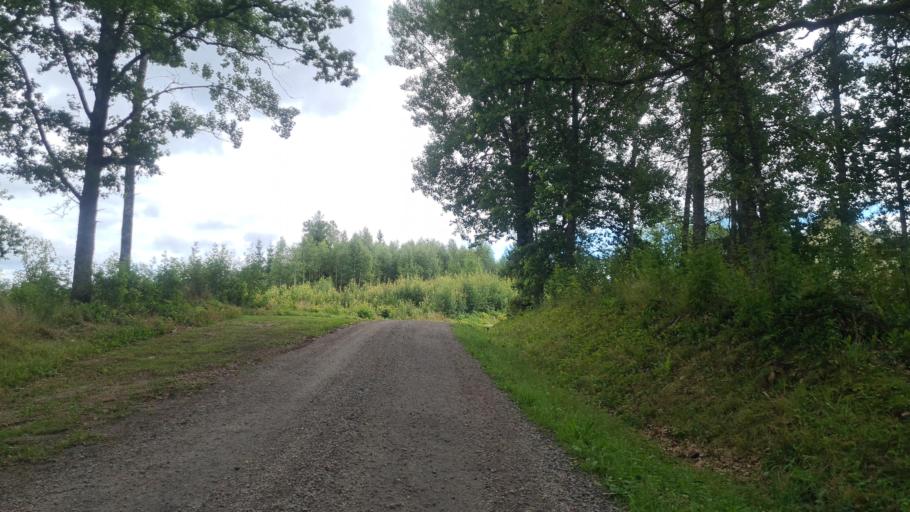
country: SE
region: Kronoberg
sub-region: Ljungby Kommun
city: Ljungby
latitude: 56.8223
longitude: 13.8626
